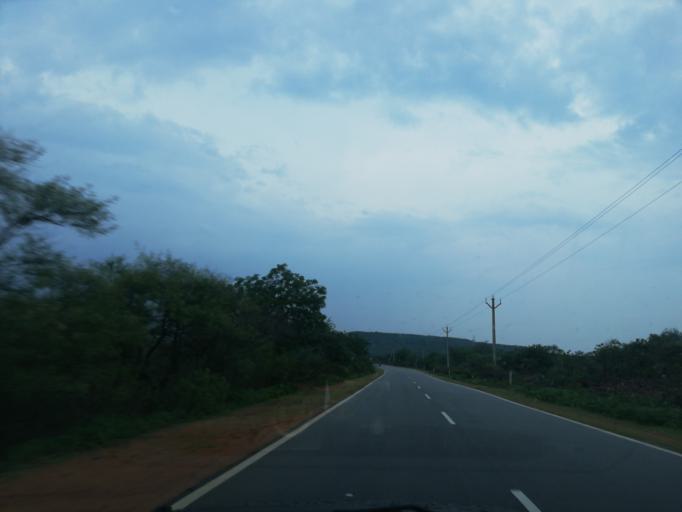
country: IN
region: Andhra Pradesh
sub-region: Guntur
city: Macherla
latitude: 16.6446
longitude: 79.2909
